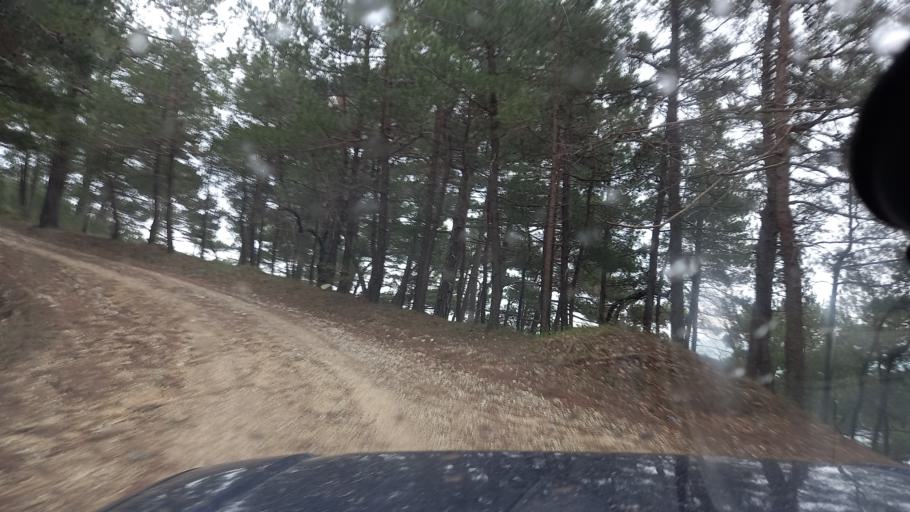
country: RU
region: Krasnodarskiy
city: Arkhipo-Osipovka
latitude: 44.3694
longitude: 38.4517
